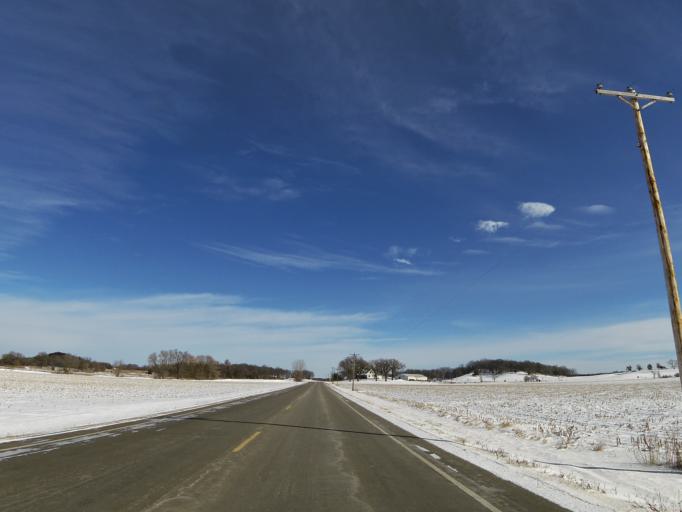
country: US
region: Wisconsin
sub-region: Pierce County
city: Prescott
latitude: 44.7992
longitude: -92.7555
